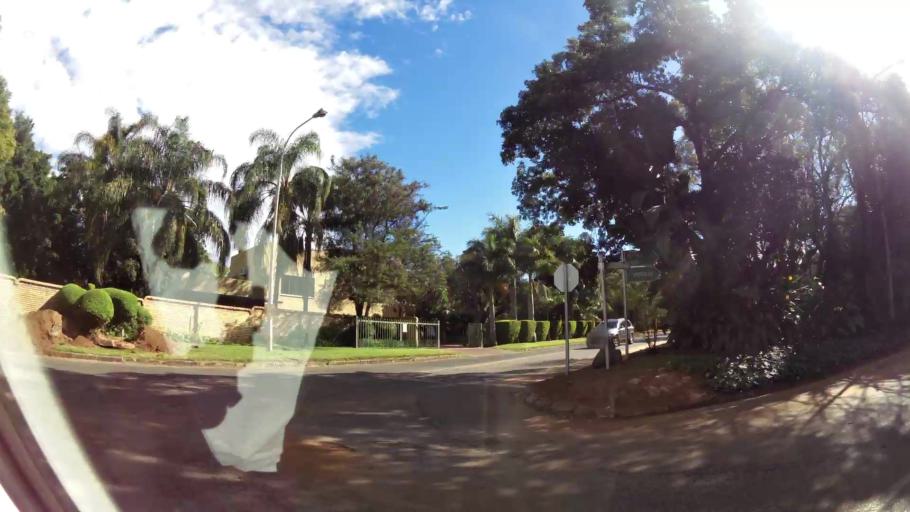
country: ZA
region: Limpopo
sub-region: Waterberg District Municipality
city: Bela-Bela
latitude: -24.8759
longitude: 28.2904
